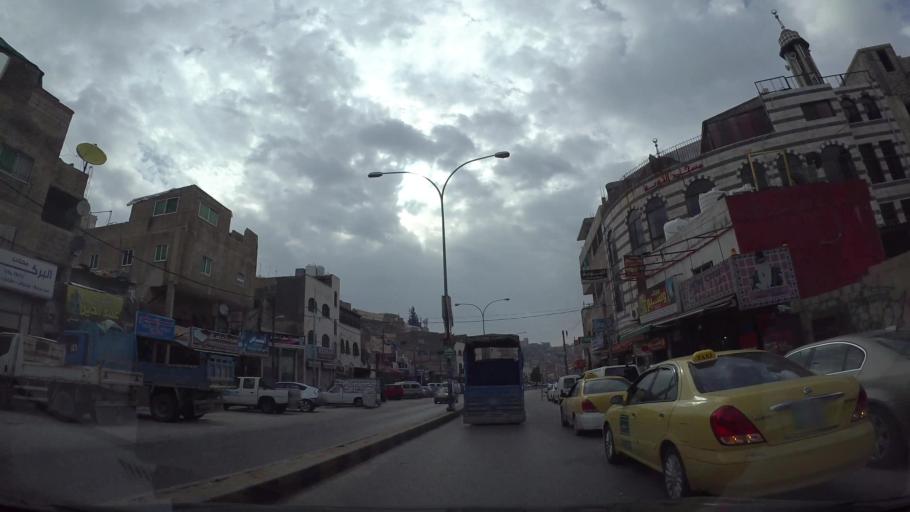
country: JO
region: Amman
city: Amman
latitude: 31.9729
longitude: 35.9239
